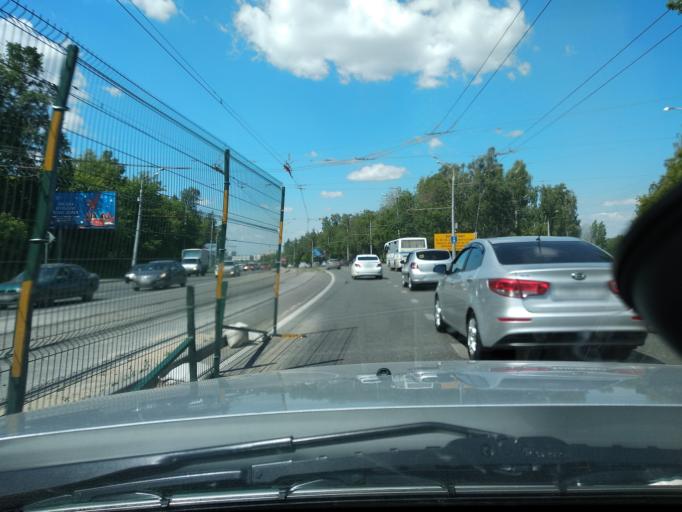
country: RU
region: Tatarstan
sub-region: Gorod Kazan'
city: Kazan
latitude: 55.8195
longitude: 49.1760
